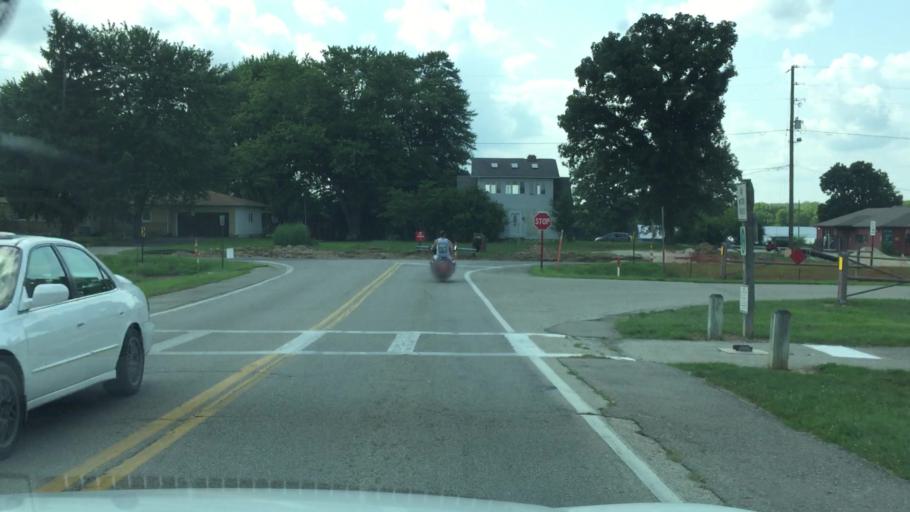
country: US
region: Ohio
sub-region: Clark County
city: Northridge
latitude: 39.9472
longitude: -83.7477
